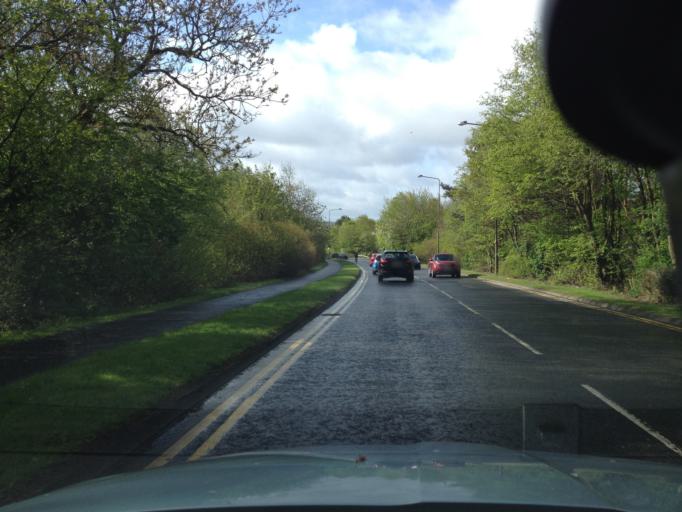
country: GB
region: Scotland
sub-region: West Lothian
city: Livingston
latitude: 55.8899
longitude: -3.5262
